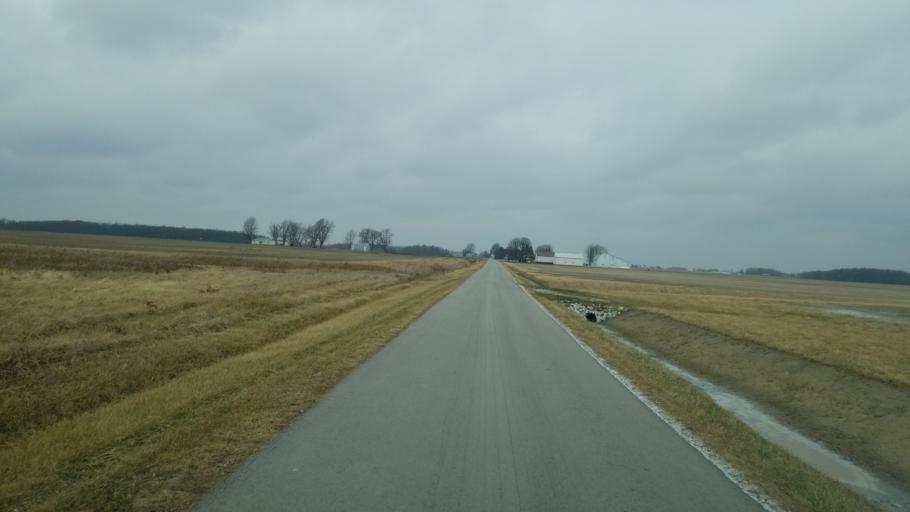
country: US
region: Ohio
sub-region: Hardin County
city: Forest
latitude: 40.7547
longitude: -83.4777
